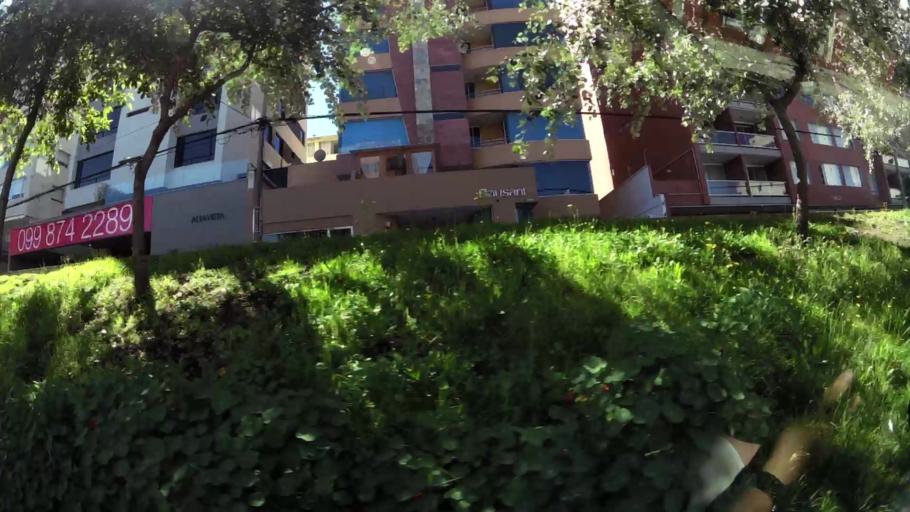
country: EC
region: Pichincha
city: Quito
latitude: -0.1784
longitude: -78.4738
